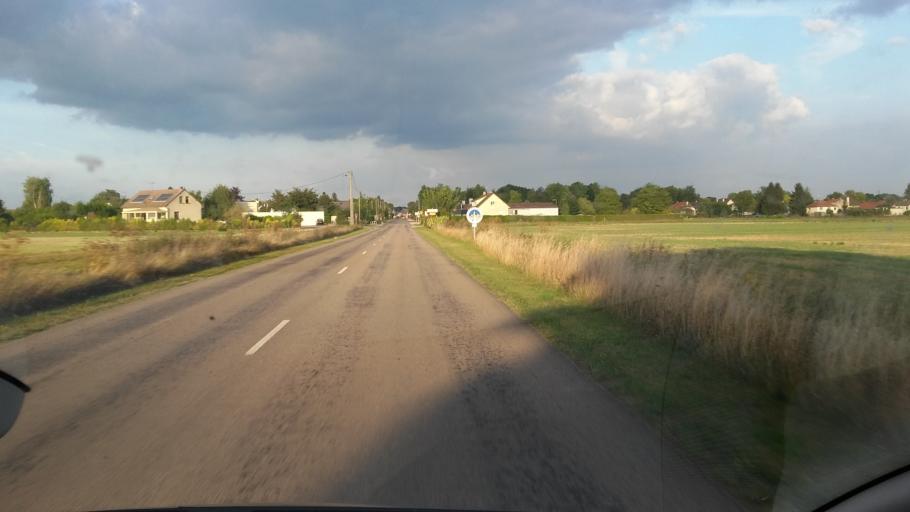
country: FR
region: Champagne-Ardenne
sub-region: Departement de la Marne
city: Fere-Champenoise
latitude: 48.7491
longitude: 3.9751
